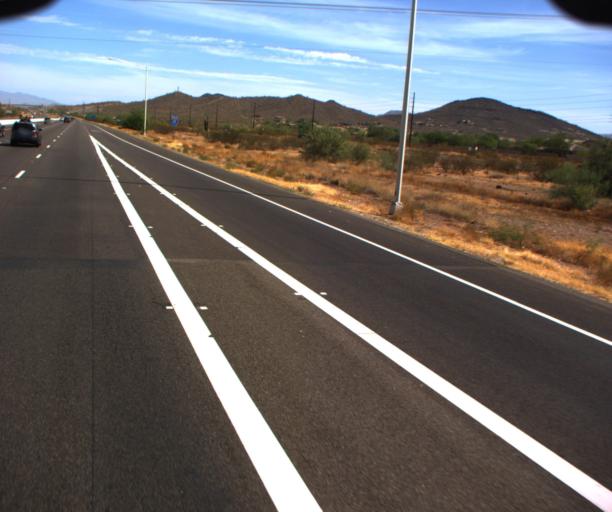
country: US
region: Arizona
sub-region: Maricopa County
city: Anthem
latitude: 33.8033
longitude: -112.1363
